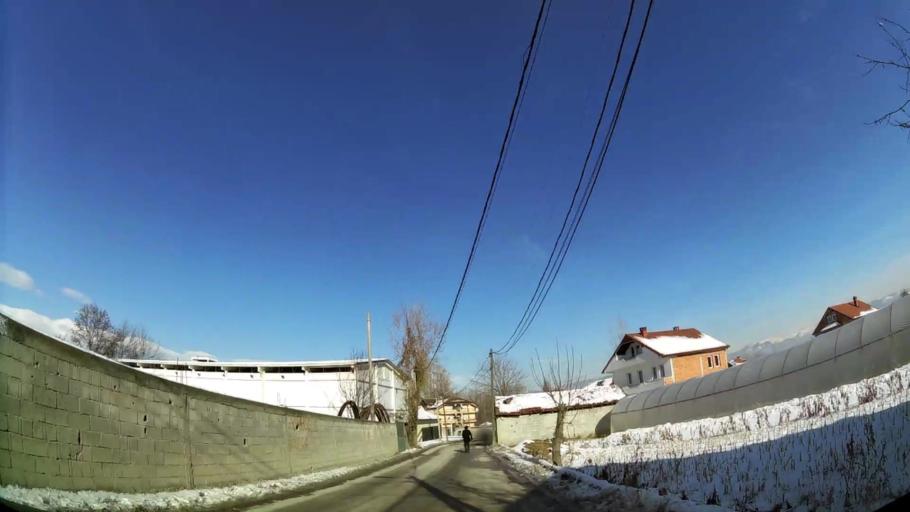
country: MK
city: Grchec
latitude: 41.9967
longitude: 21.3433
